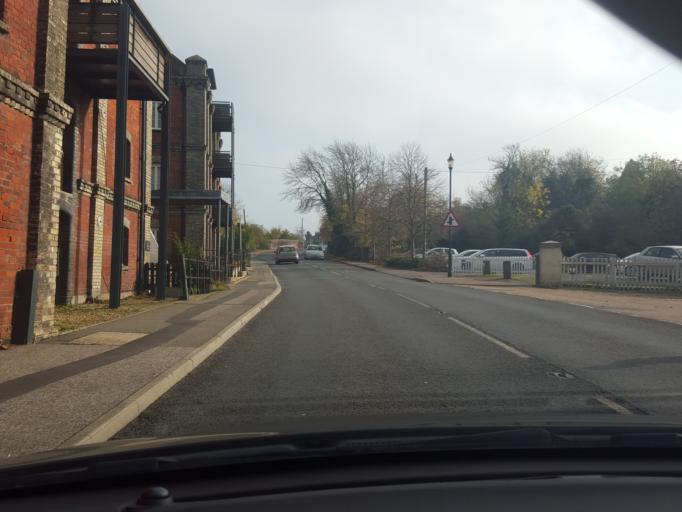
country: GB
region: England
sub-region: Essex
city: Mistley
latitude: 51.9441
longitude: 1.0813
